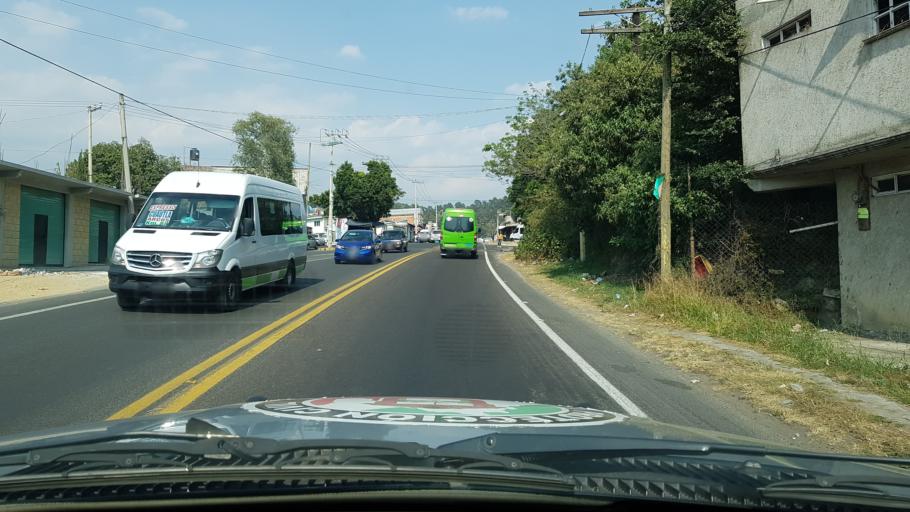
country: MX
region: Mexico
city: Tepetlixpa
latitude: 19.0242
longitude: -98.8220
